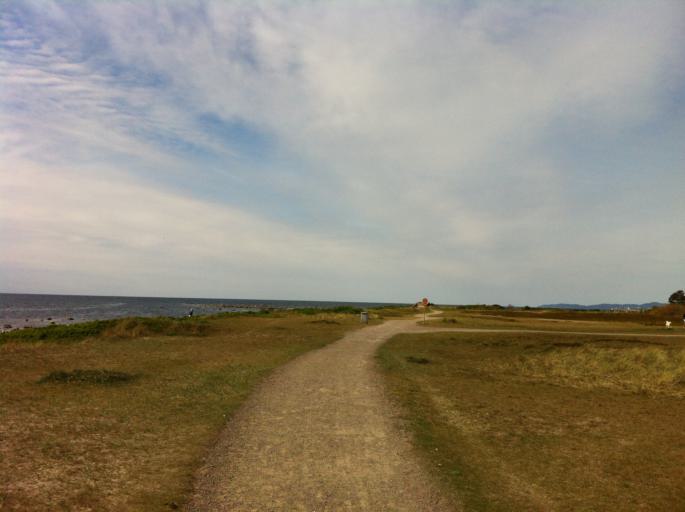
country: SE
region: Skane
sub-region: Hoganas Kommun
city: Hoganas
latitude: 56.1533
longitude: 12.5679
